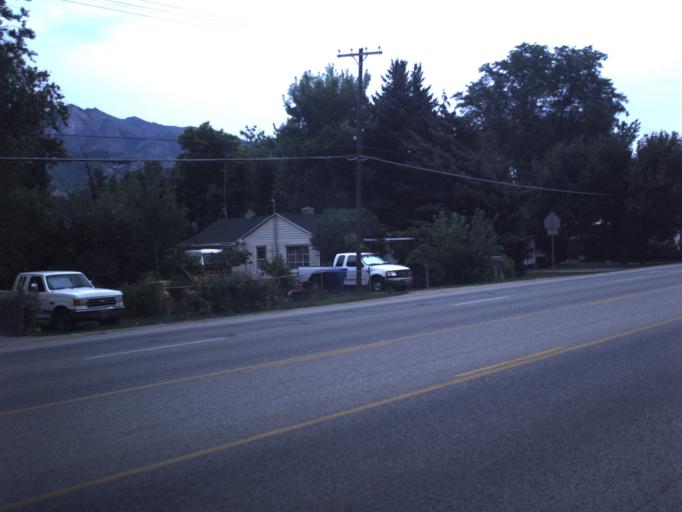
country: US
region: Utah
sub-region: Weber County
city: Harrisville
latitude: 41.2580
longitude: -111.9780
